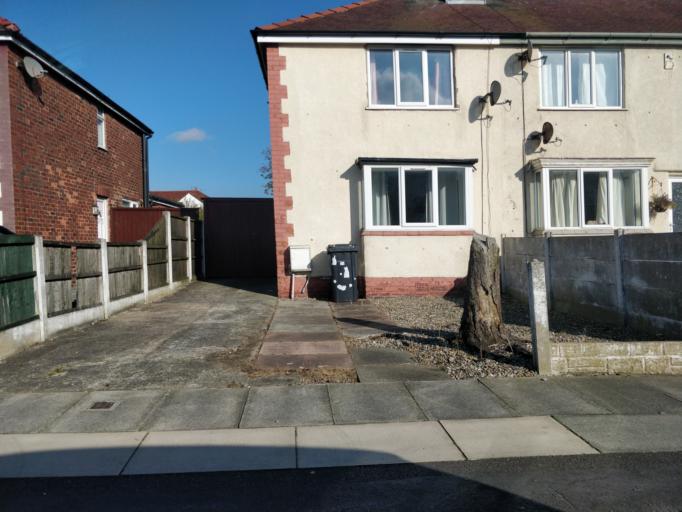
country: GB
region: England
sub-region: Lancashire
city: Banks
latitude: 53.6705
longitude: -2.9531
